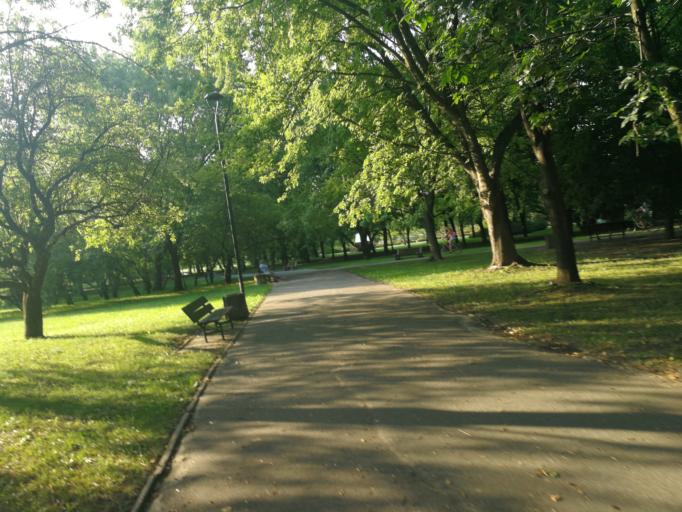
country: PL
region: Masovian Voivodeship
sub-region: Warszawa
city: Targowek
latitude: 52.2897
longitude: 21.0372
